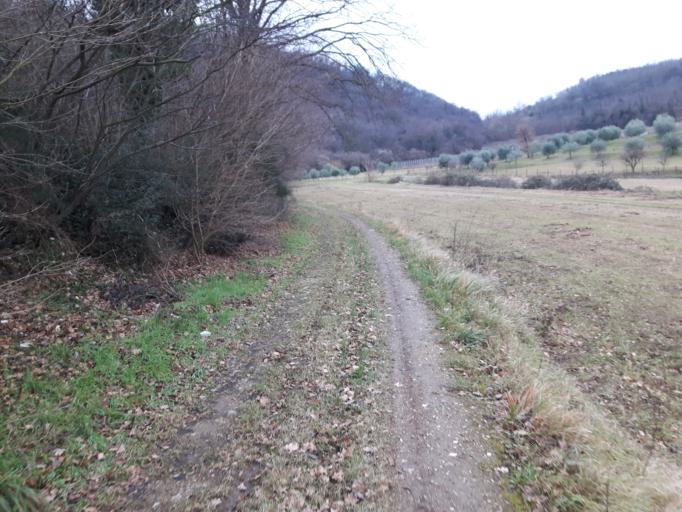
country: IT
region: Veneto
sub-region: Provincia di Padova
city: Arqua Petrarca
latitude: 45.2772
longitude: 11.7399
